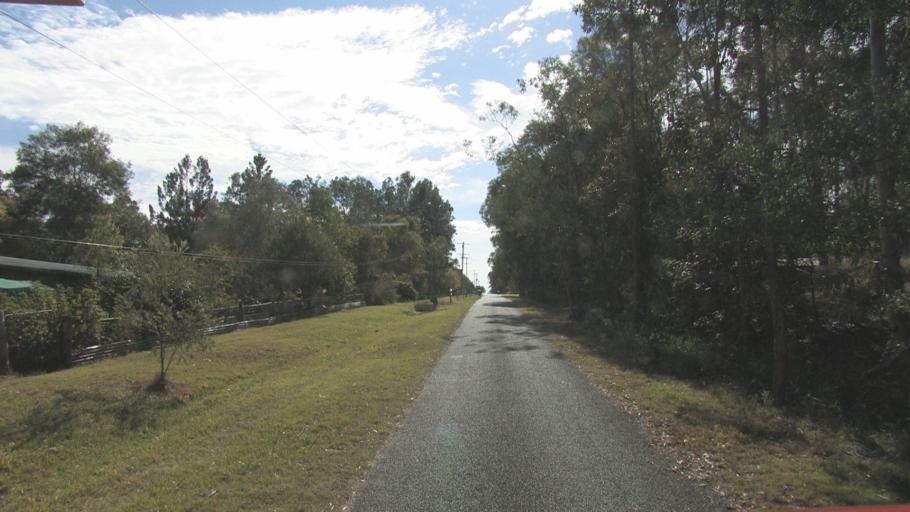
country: AU
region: Queensland
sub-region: Logan
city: North Maclean
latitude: -27.7809
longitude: 152.9903
